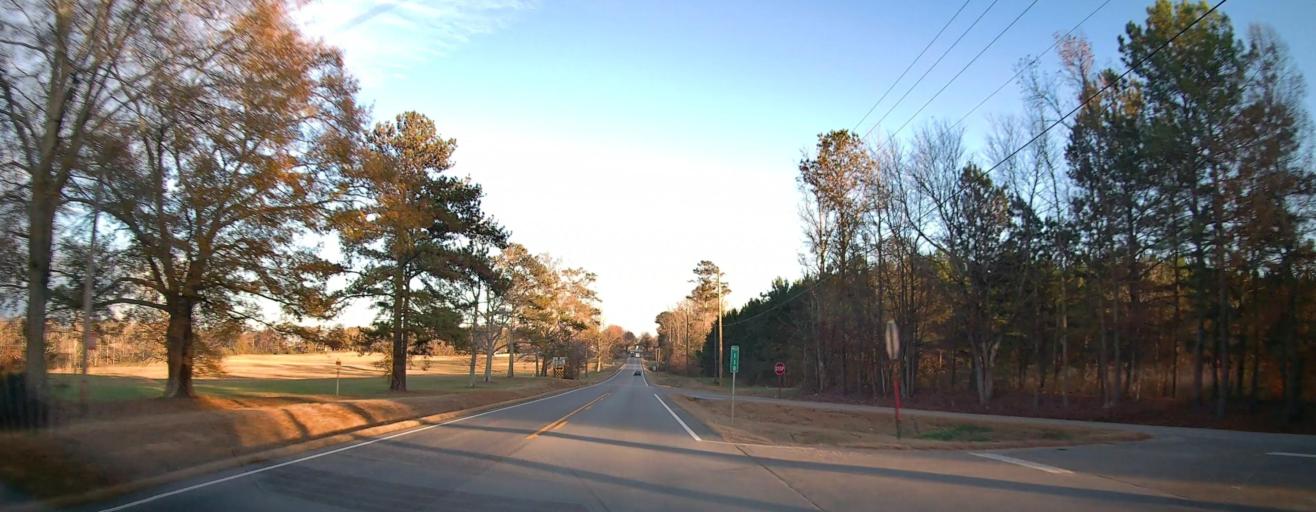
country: US
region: Alabama
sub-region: Saint Clair County
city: Steele
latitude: 34.0579
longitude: -86.2217
